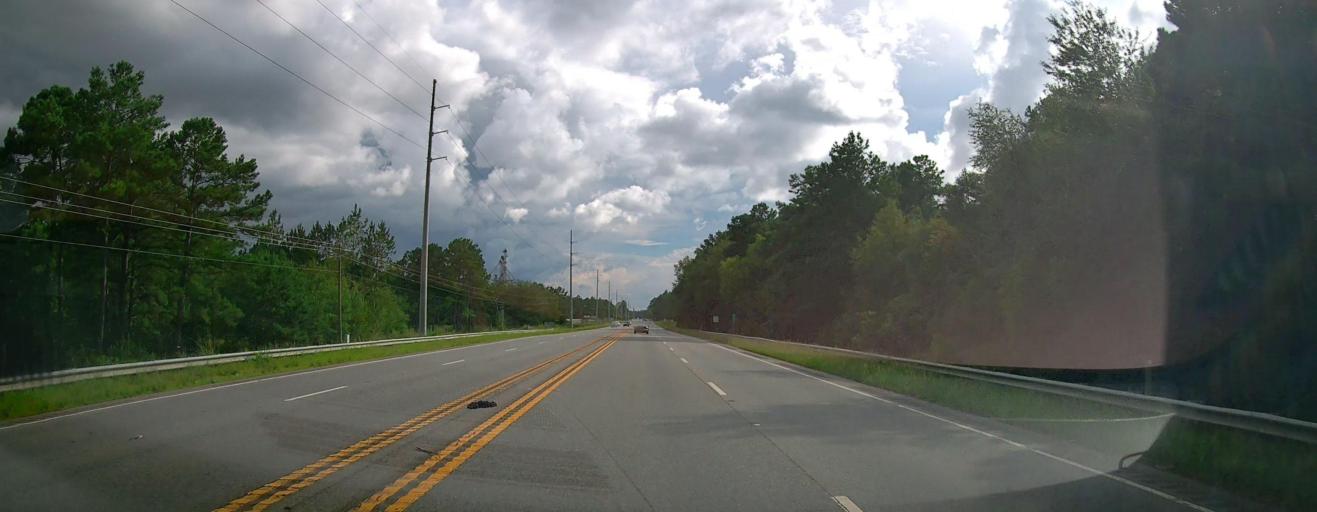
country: US
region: Georgia
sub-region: Pierce County
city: Blackshear
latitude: 31.3974
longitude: -82.1275
